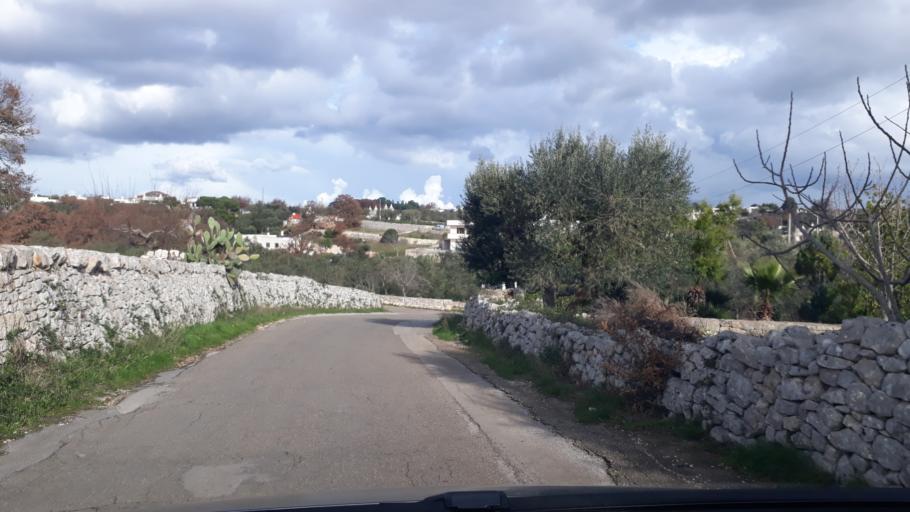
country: IT
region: Apulia
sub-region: Provincia di Brindisi
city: Cisternino
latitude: 40.7192
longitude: 17.4250
